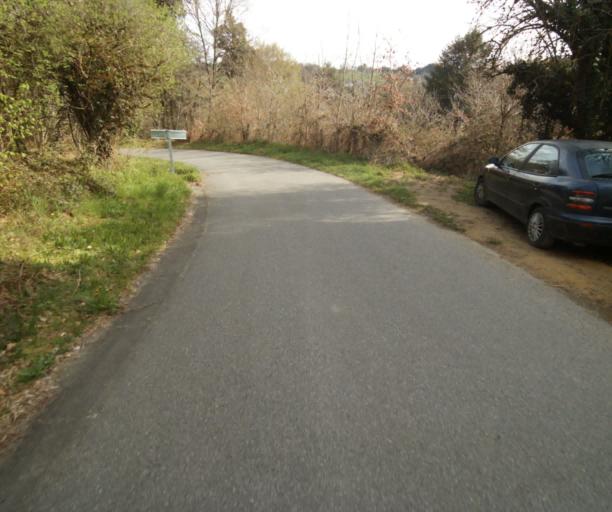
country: FR
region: Limousin
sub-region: Departement de la Correze
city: Correze
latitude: 45.3428
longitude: 1.8553
